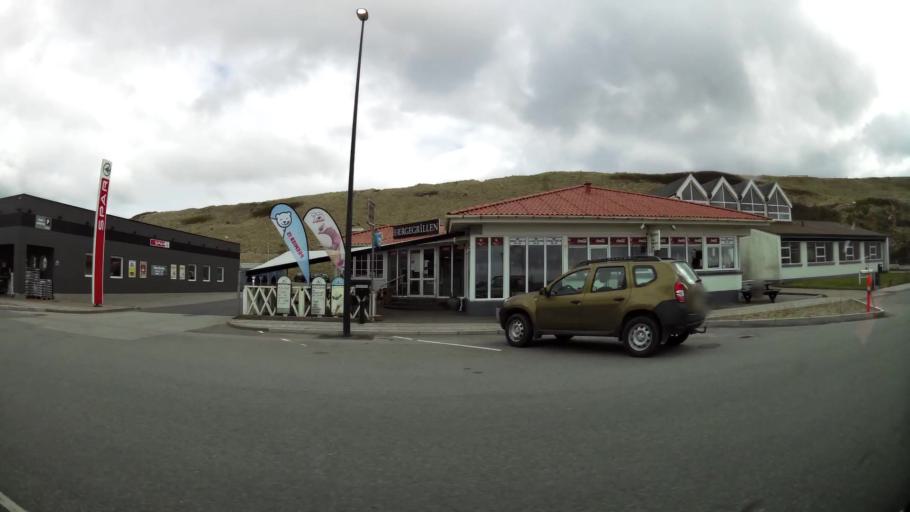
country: DK
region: North Denmark
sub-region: Thisted Kommune
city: Hanstholm
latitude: 57.1182
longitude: 8.5966
